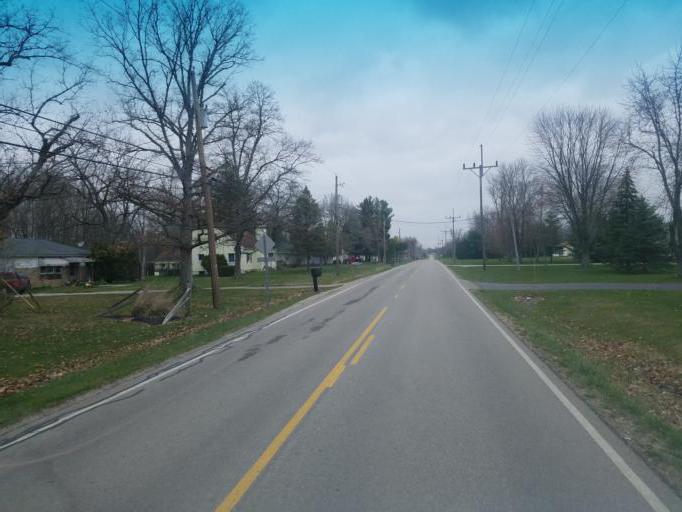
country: US
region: Ohio
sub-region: Marion County
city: Marion
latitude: 40.5355
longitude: -83.1507
